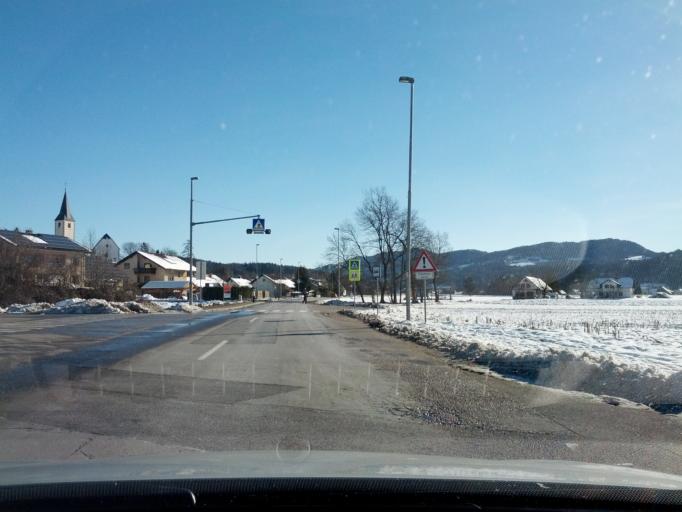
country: SI
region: Domzale
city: Dob
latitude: 46.1515
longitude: 14.6548
